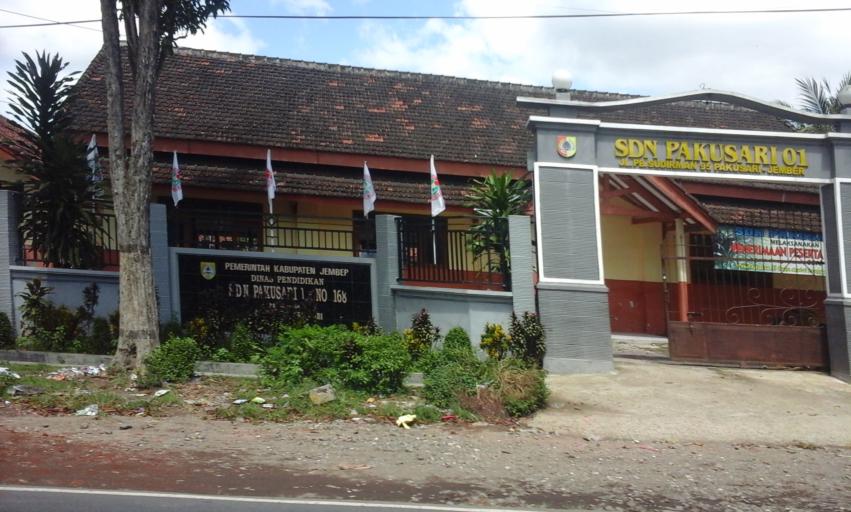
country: ID
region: East Java
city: Pakusari
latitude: -8.1768
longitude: 113.7791
